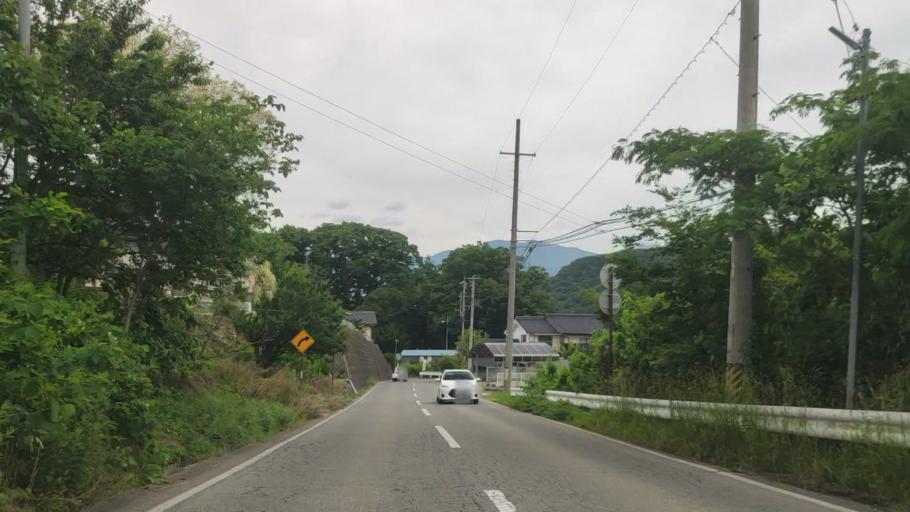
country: JP
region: Nagano
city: Kamimaruko
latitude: 36.3286
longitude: 138.3445
